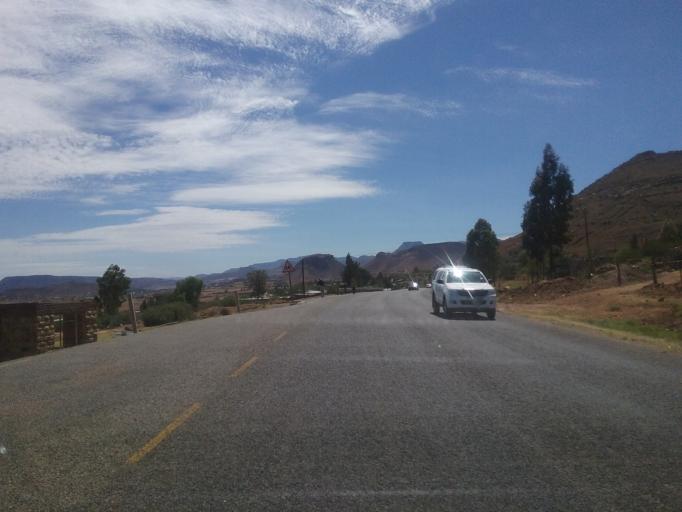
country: LS
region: Mohale's Hoek District
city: Mohale's Hoek
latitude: -30.1879
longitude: 27.4182
